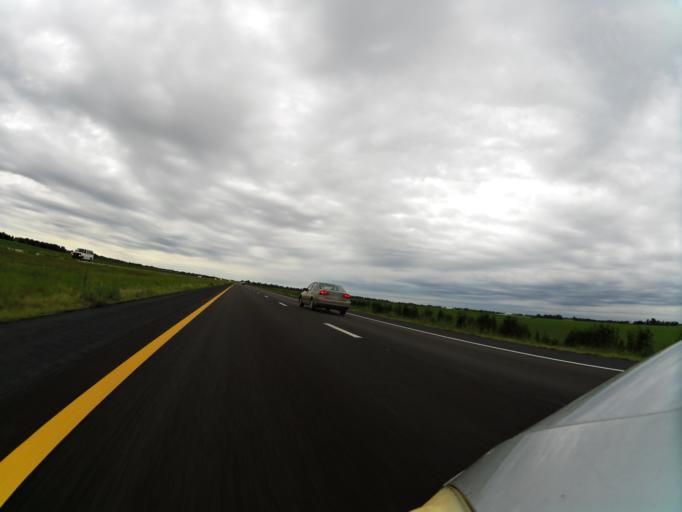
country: US
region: Kansas
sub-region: Reno County
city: Haven
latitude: 37.8762
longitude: -97.6556
